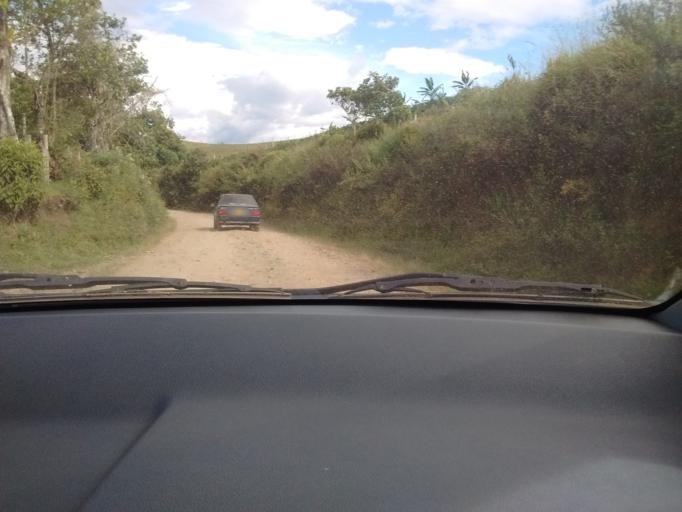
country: CO
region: Cauca
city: El Tambo
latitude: 2.4622
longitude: -76.8233
